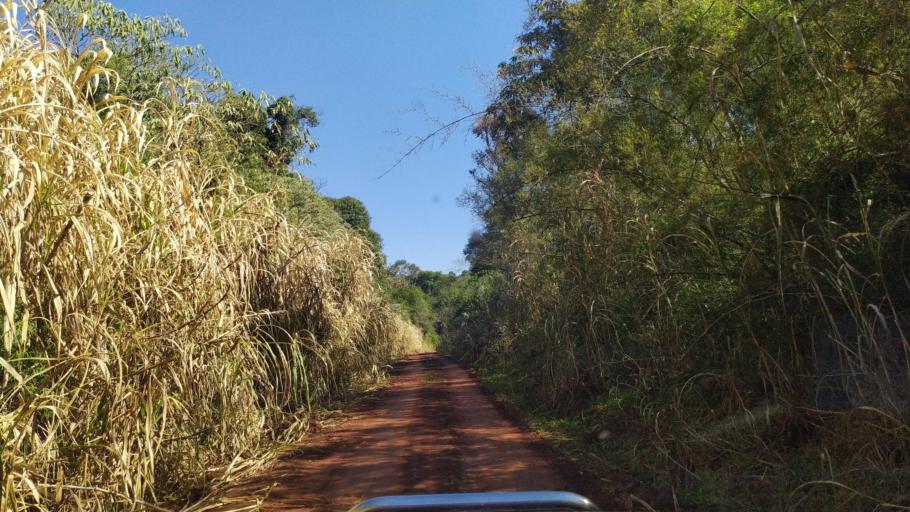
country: AR
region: Misiones
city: El Alcazar
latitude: -26.7522
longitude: -54.6068
